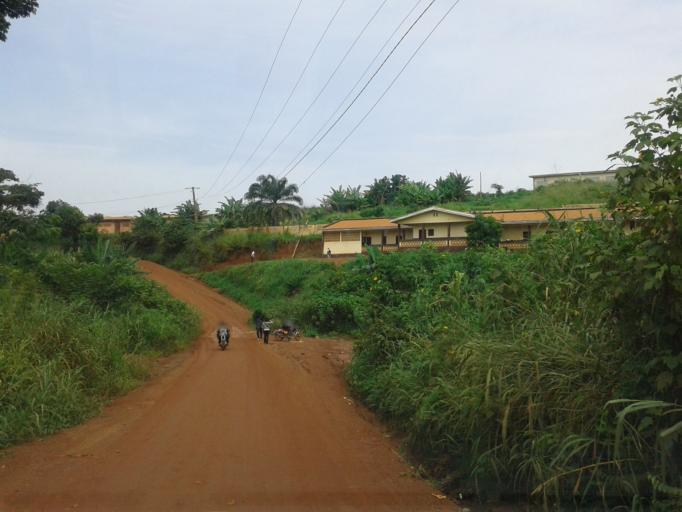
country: CM
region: Centre
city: Yaounde
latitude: 3.9236
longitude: 11.5072
